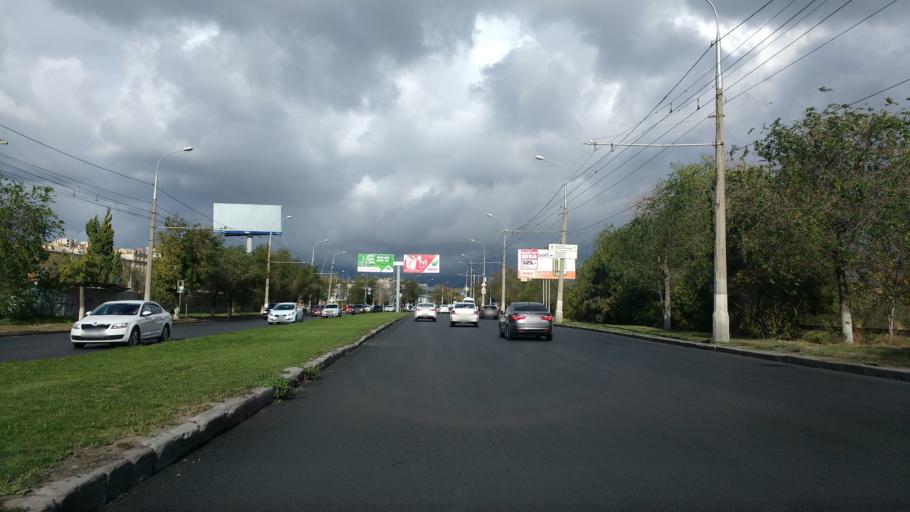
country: RU
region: Volgograd
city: Krasnoslobodsk
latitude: 48.7696
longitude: 44.5657
